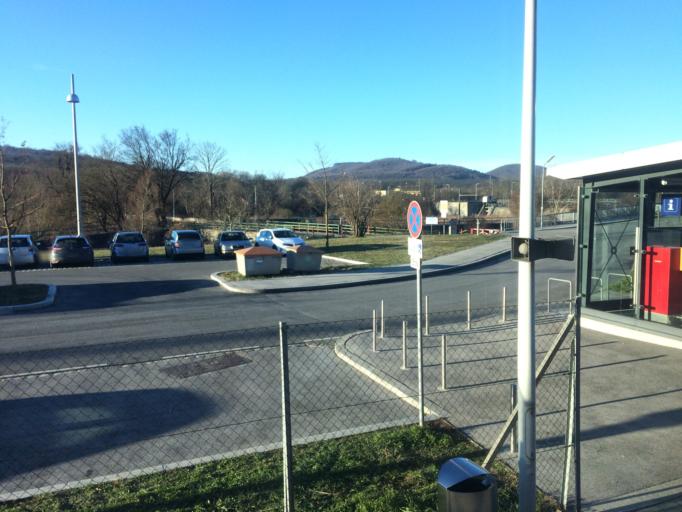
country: AT
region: Lower Austria
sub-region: Politischer Bezirk Wien-Umgebung
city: Purkersdorf
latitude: 48.2045
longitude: 16.2365
